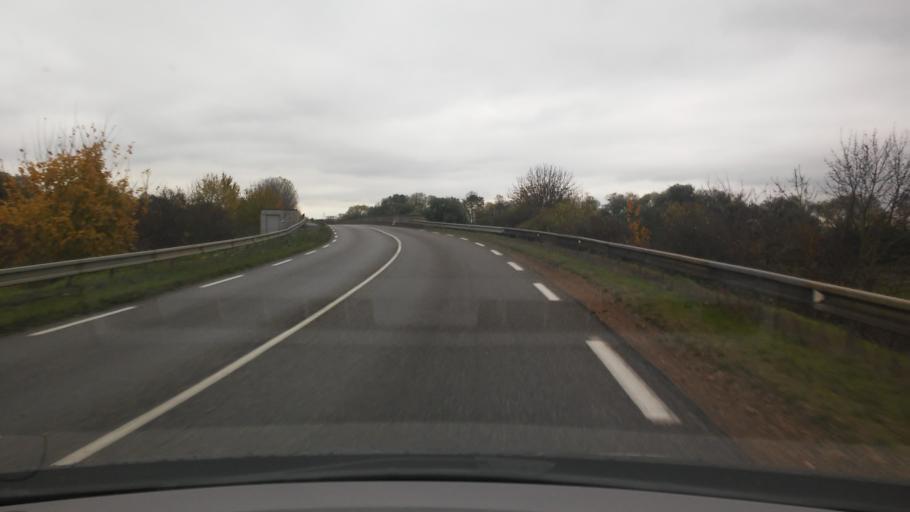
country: FR
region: Lorraine
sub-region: Departement de la Moselle
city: Mondelange
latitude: 49.2564
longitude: 6.1832
